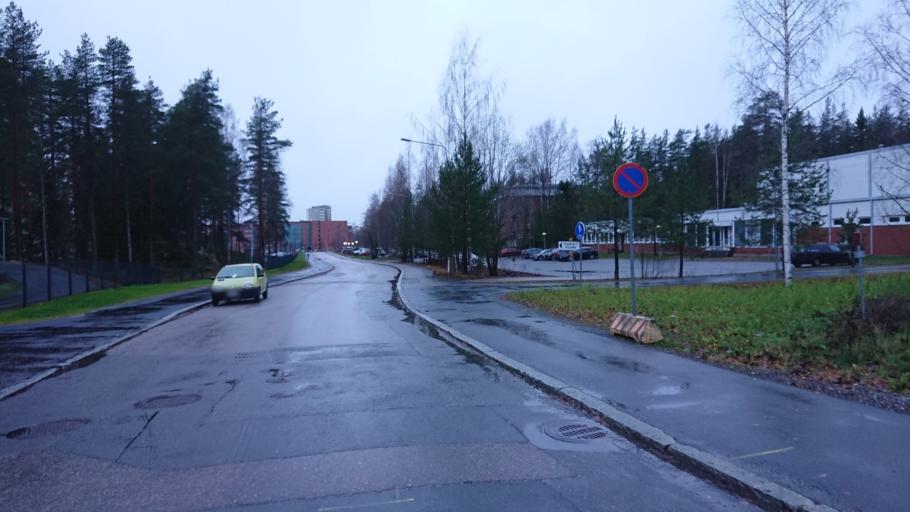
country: FI
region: Pirkanmaa
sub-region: Tampere
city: Tampere
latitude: 61.4551
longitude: 23.8566
